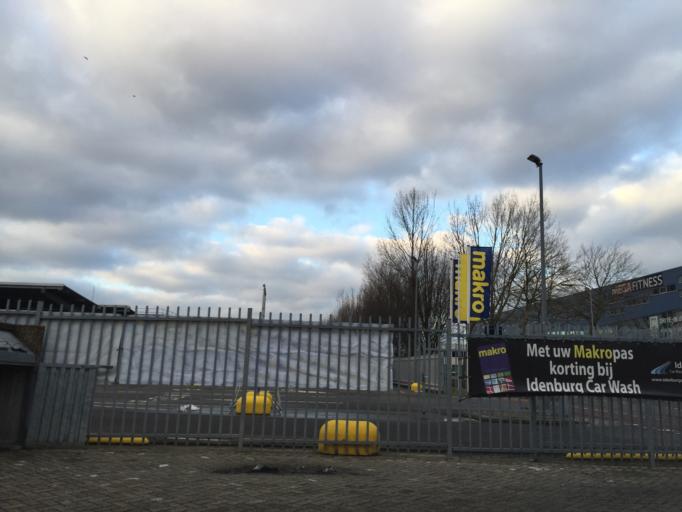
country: NL
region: South Holland
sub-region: Gemeente Delft
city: Delft
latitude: 51.9827
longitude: 4.3719
